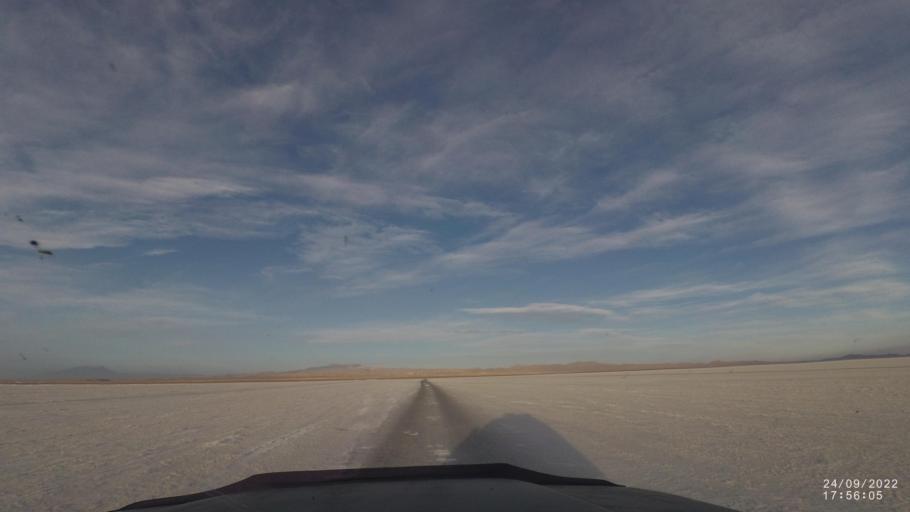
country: BO
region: Potosi
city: Colchani
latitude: -20.3252
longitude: -67.0193
